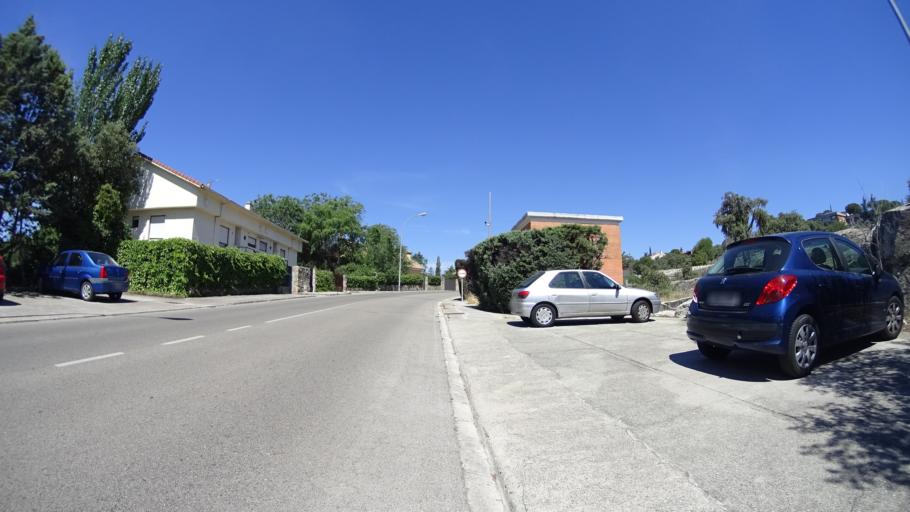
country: ES
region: Madrid
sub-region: Provincia de Madrid
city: Torrelodones
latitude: 40.6056
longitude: -3.9405
